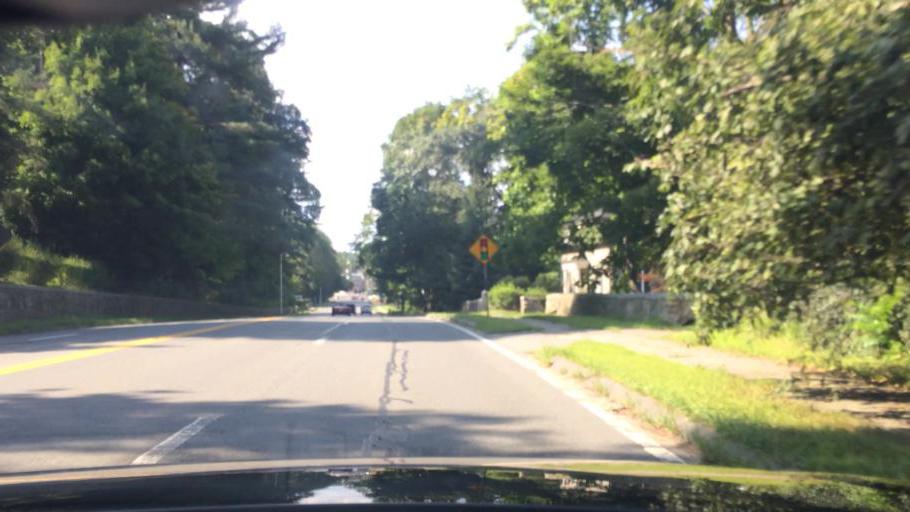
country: US
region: Massachusetts
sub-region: Essex County
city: Andover
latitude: 42.6682
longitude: -71.1480
